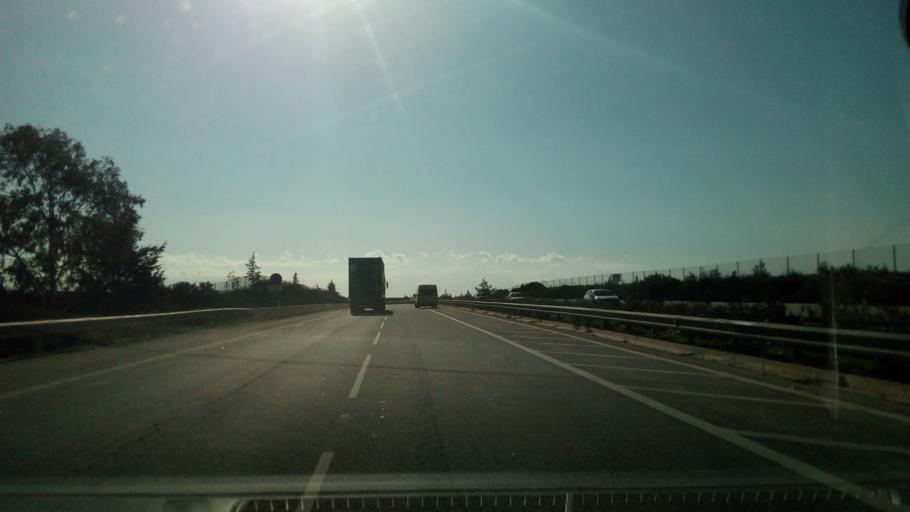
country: CY
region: Larnaka
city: Xylotymbou
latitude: 34.9965
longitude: 33.7575
